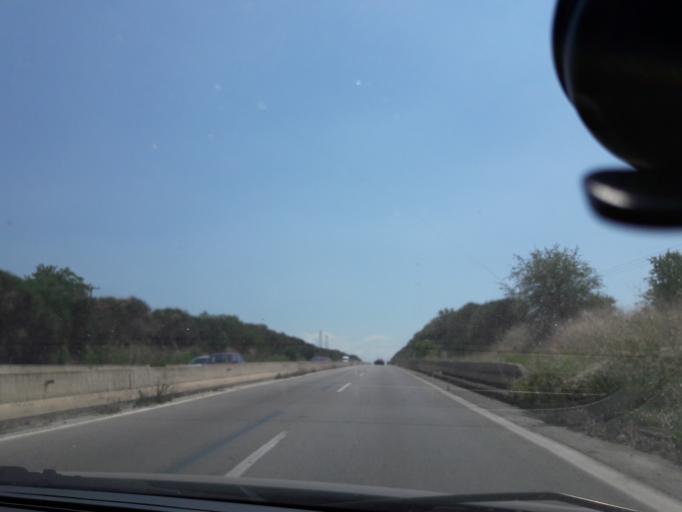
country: GR
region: Central Macedonia
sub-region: Nomos Chalkidikis
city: Nea Kallikrateia
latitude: 40.3024
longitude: 23.1332
